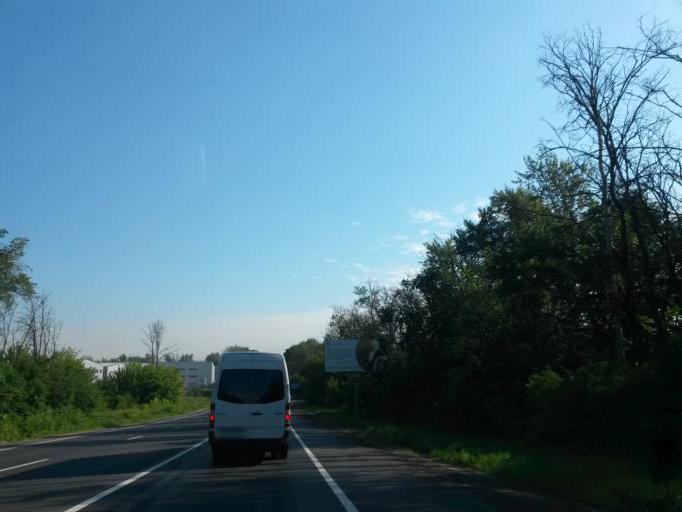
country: RU
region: Moskovskaya
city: Gorki-Leninskiye
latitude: 55.5138
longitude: 37.7580
